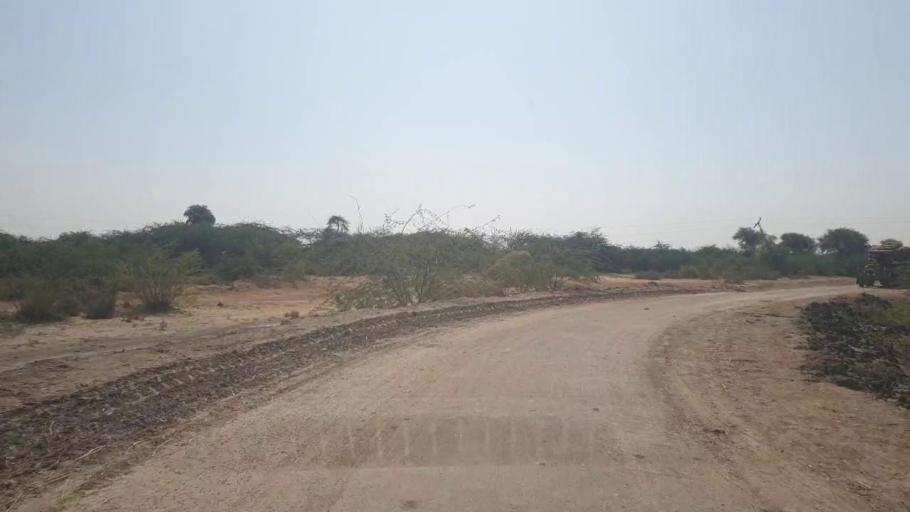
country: PK
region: Sindh
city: Badin
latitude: 24.6468
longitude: 68.9167
